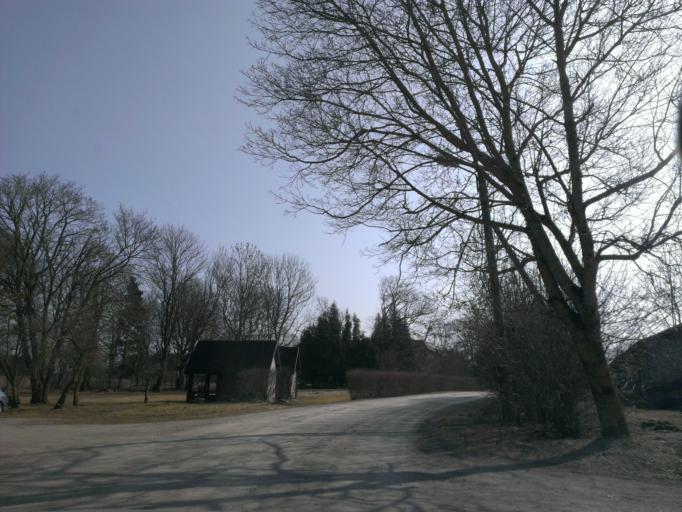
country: EE
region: Saare
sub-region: Orissaare vald
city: Orissaare
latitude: 58.5595
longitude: 23.0876
